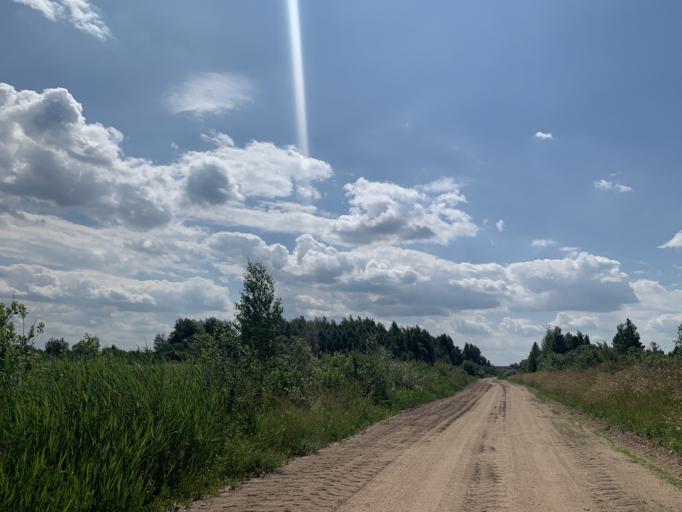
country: BY
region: Minsk
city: Nyasvizh
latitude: 53.2225
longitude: 26.7407
